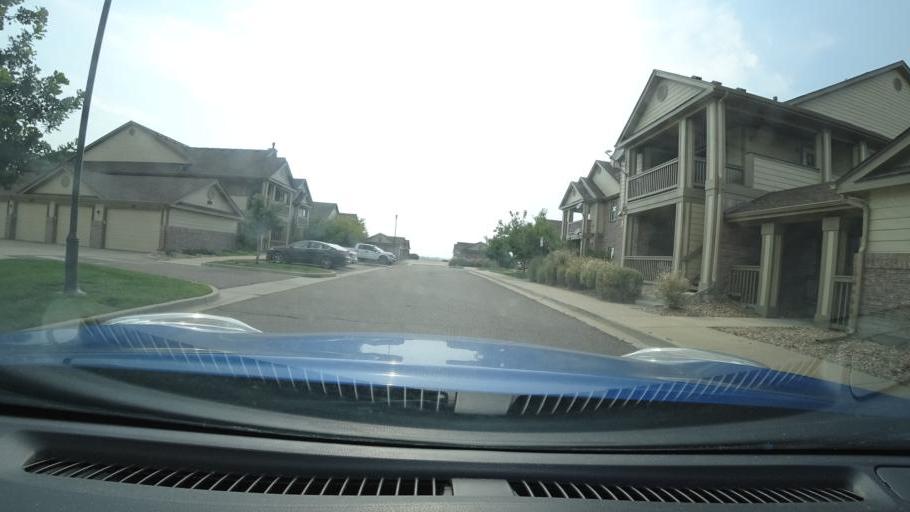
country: US
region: Colorado
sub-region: Adams County
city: Aurora
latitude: 39.7243
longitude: -104.7146
